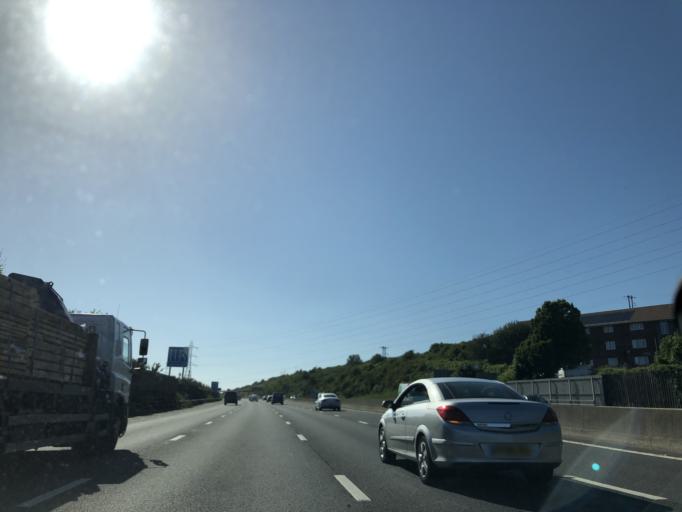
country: GB
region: England
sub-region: Portsmouth
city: Cosham
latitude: 50.8545
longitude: -1.1127
